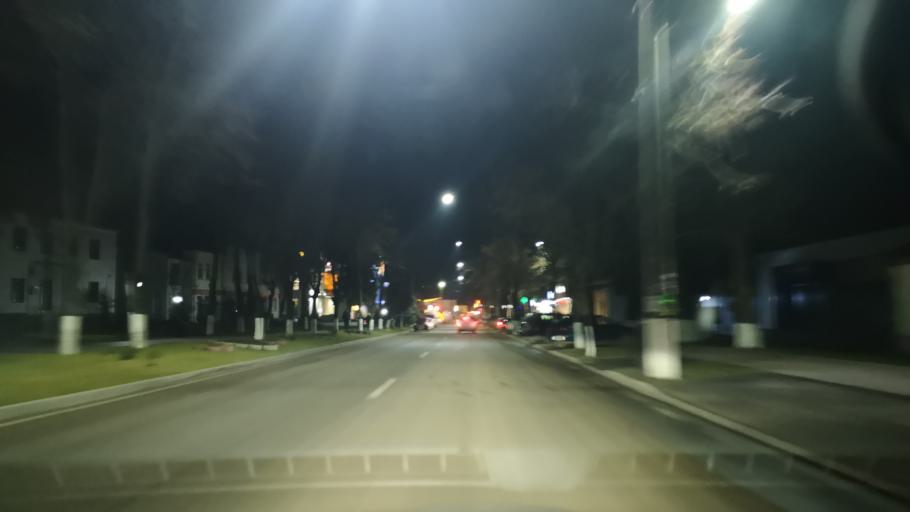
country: MD
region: Orhei
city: Orhei
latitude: 47.3805
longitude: 28.8250
